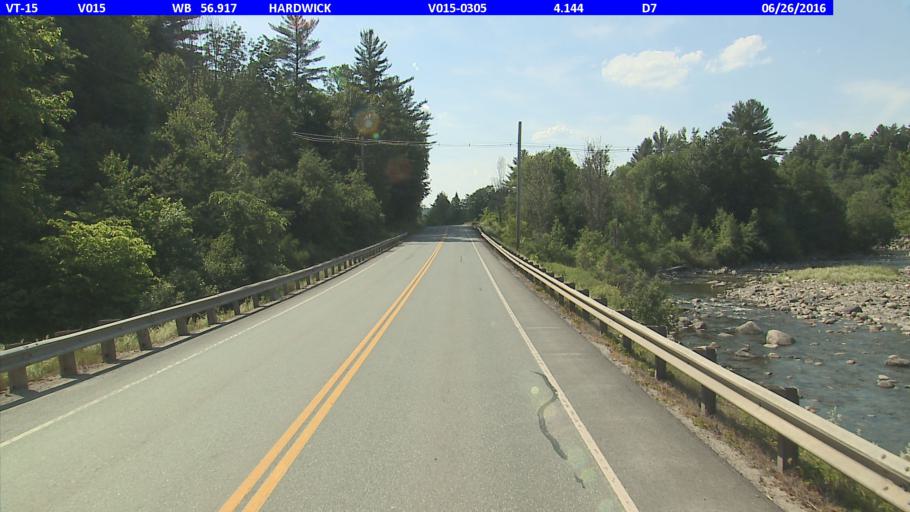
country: US
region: Vermont
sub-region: Caledonia County
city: Hardwick
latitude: 44.5023
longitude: -72.3541
